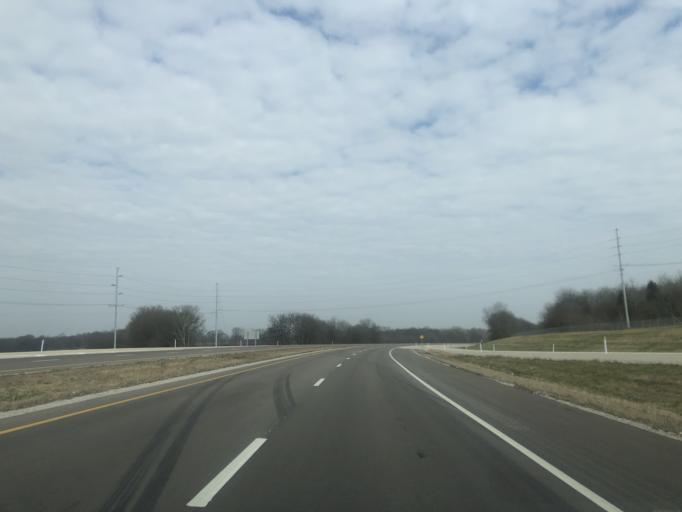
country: US
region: Tennessee
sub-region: Maury County
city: Mount Pleasant
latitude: 35.5465
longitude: -87.2193
